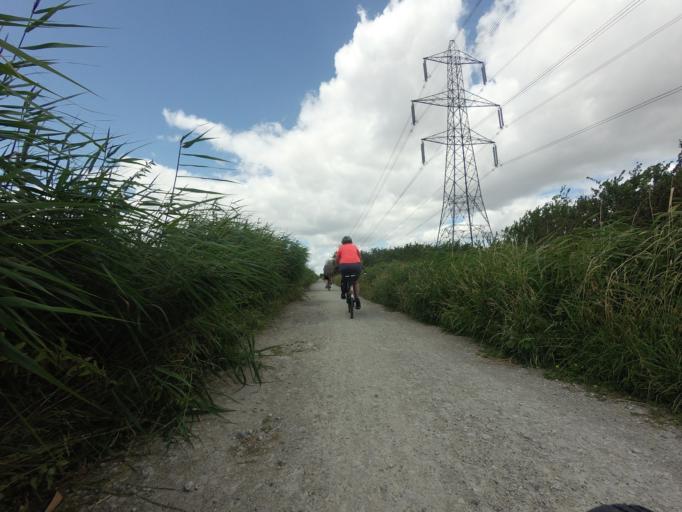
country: GB
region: England
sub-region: Kent
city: Gravesend
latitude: 51.4390
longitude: 0.4178
